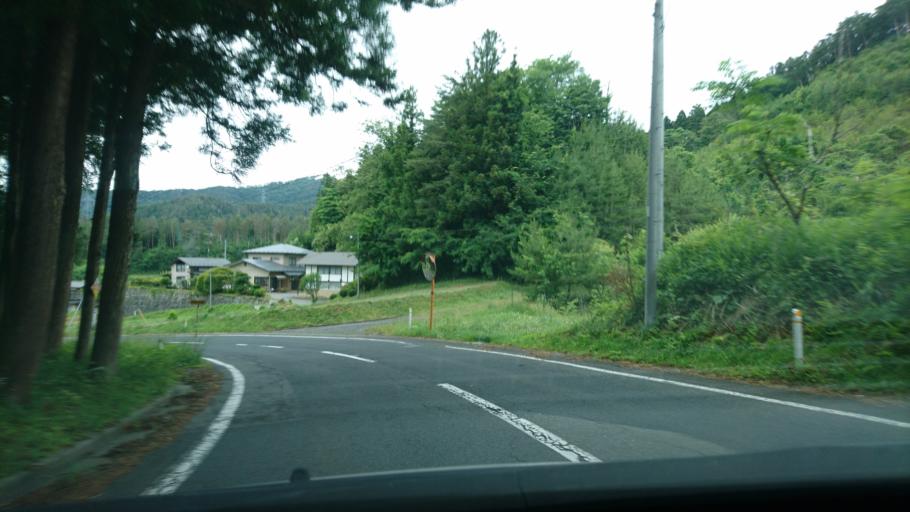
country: JP
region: Iwate
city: Ichinoseki
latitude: 38.9450
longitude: 141.2717
